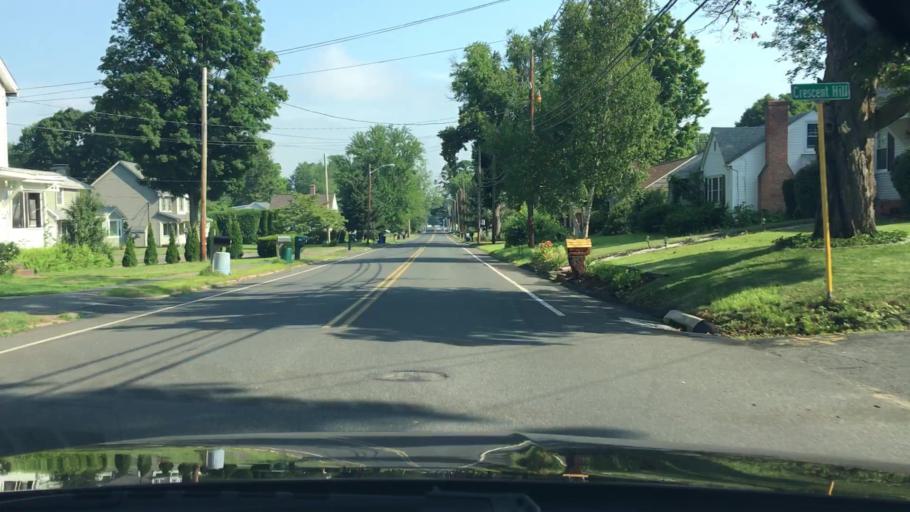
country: US
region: Massachusetts
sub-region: Hampden County
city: East Longmeadow
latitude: 42.0606
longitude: -72.5122
